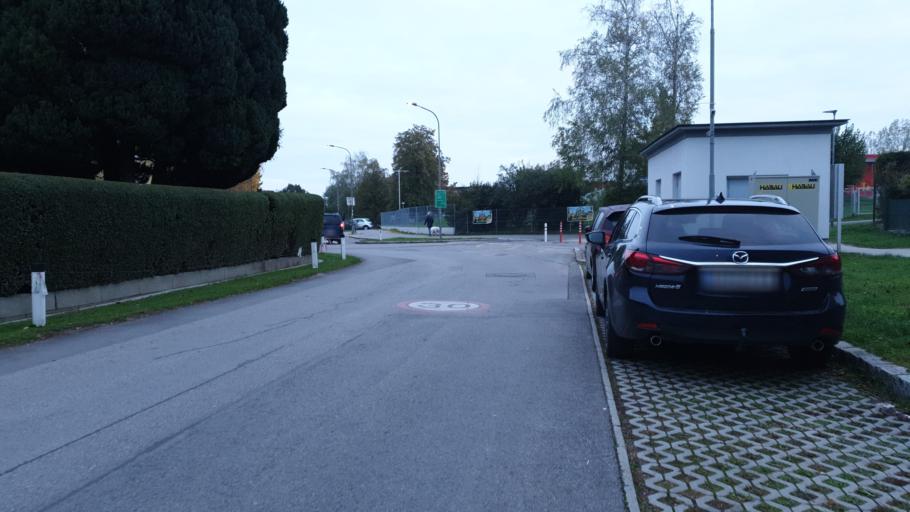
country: AT
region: Lower Austria
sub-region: Politischer Bezirk Wien-Umgebung
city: Gerasdorf bei Wien
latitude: 48.2953
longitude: 16.4585
